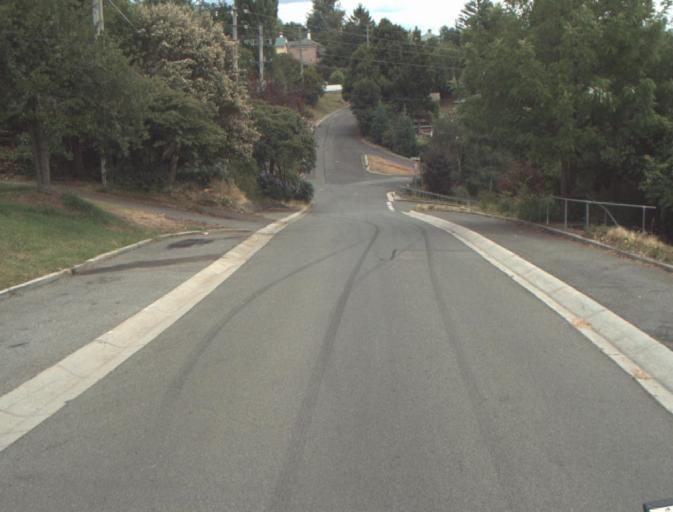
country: AU
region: Tasmania
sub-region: Launceston
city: Launceston
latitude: -41.4392
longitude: 147.1238
